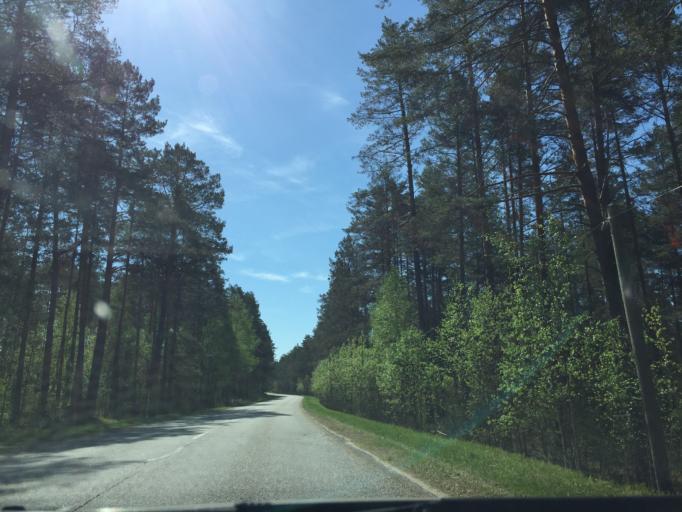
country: LV
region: Garkalne
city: Garkalne
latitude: 57.0260
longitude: 24.4310
